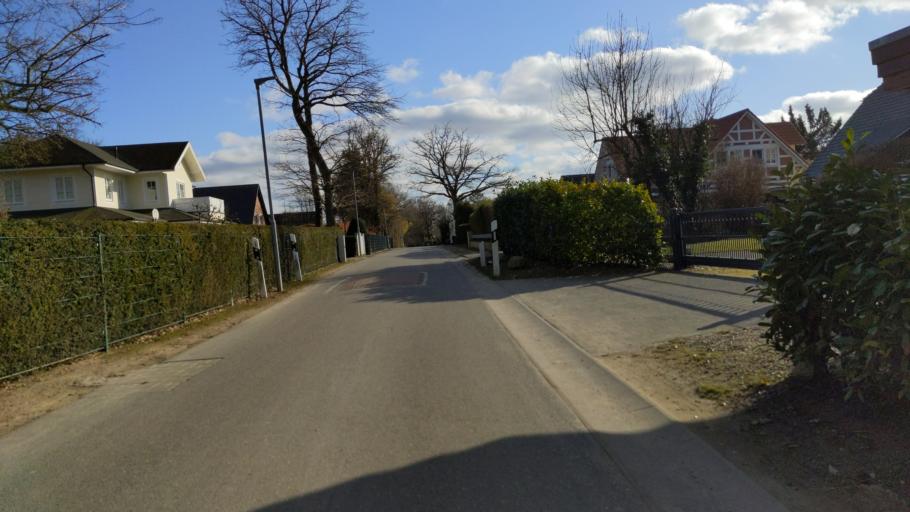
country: DE
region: Schleswig-Holstein
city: Timmendorfer Strand
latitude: 54.0025
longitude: 10.7546
